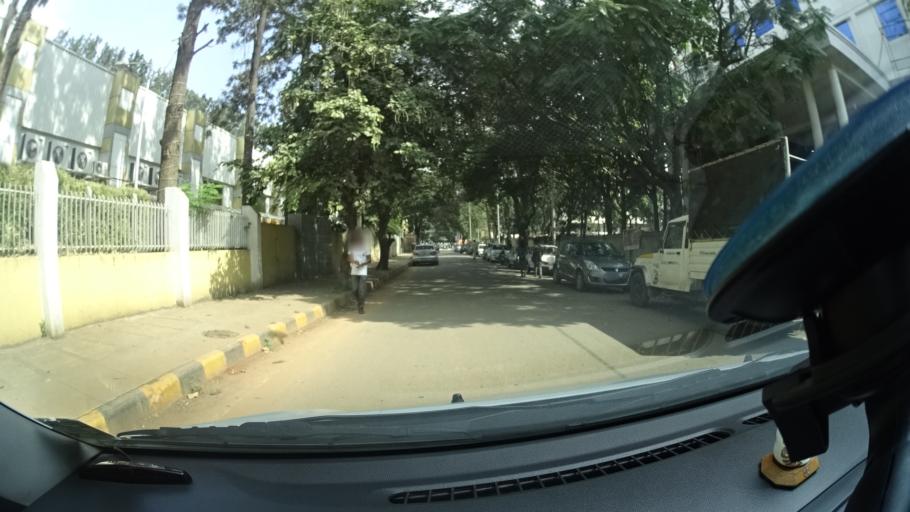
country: IN
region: Karnataka
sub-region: Bangalore Urban
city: Yelahanka
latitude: 13.0974
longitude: 77.5901
